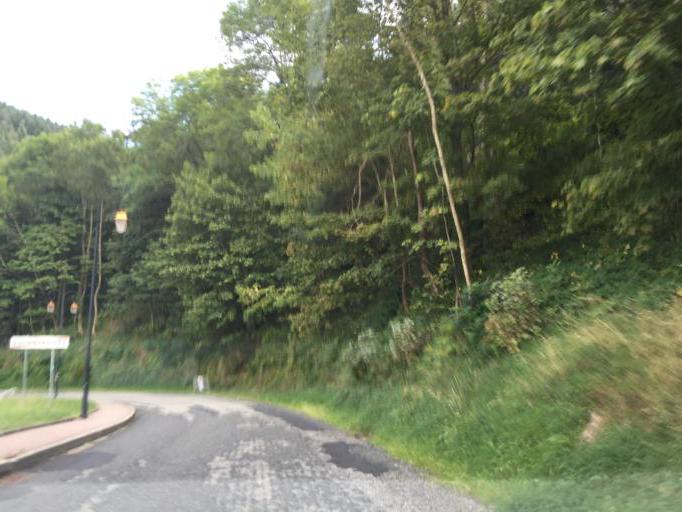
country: FR
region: Rhone-Alpes
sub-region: Departement de la Loire
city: Saint-Jean-Bonnefonds
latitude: 45.4095
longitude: 4.4483
